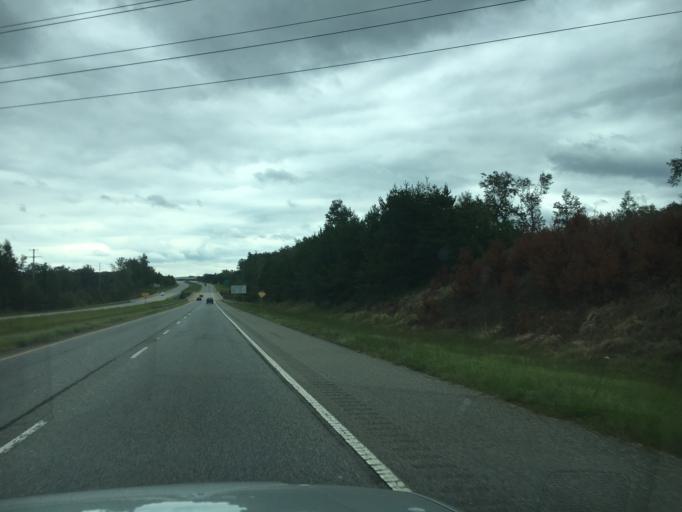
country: US
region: South Carolina
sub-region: Greenville County
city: Mauldin
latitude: 34.7344
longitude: -82.3260
